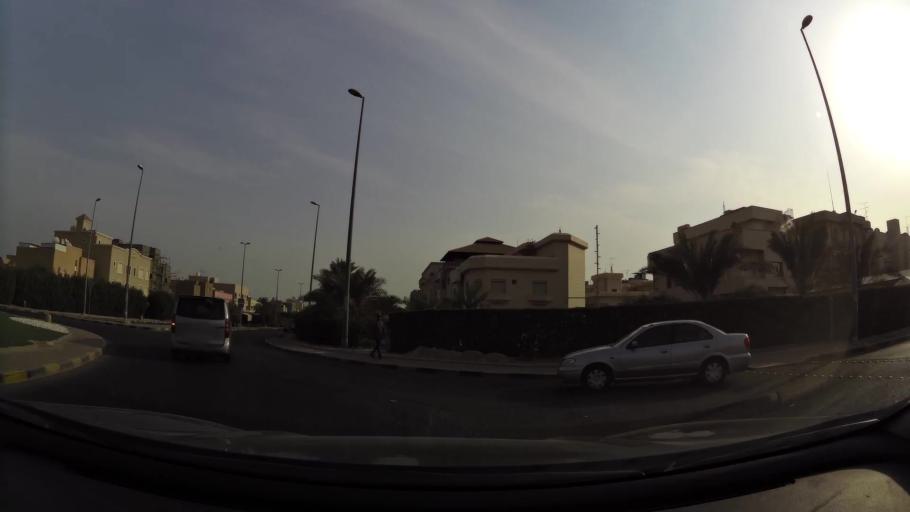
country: KW
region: Mubarak al Kabir
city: Sabah as Salim
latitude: 29.2252
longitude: 48.0600
